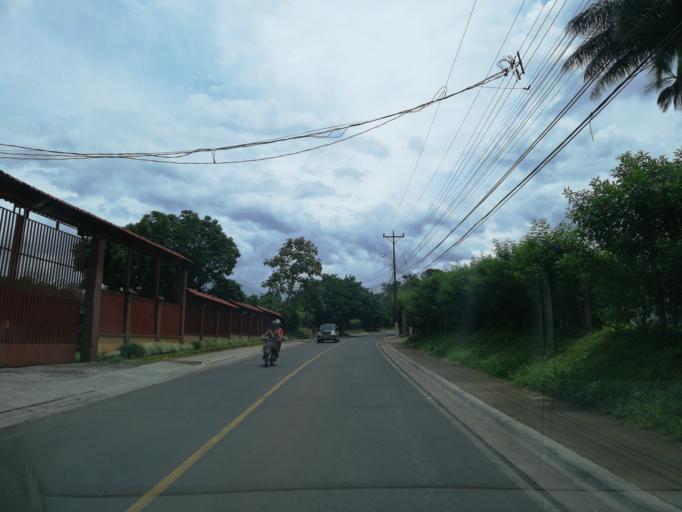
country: CR
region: Alajuela
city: Alajuela
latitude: 10.0213
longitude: -84.1973
